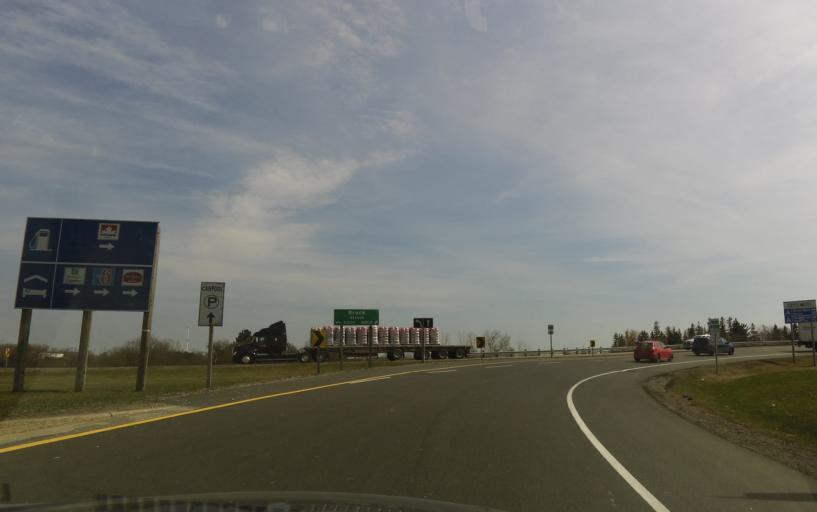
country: CA
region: Ontario
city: Oshawa
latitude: 43.8658
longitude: -78.9346
